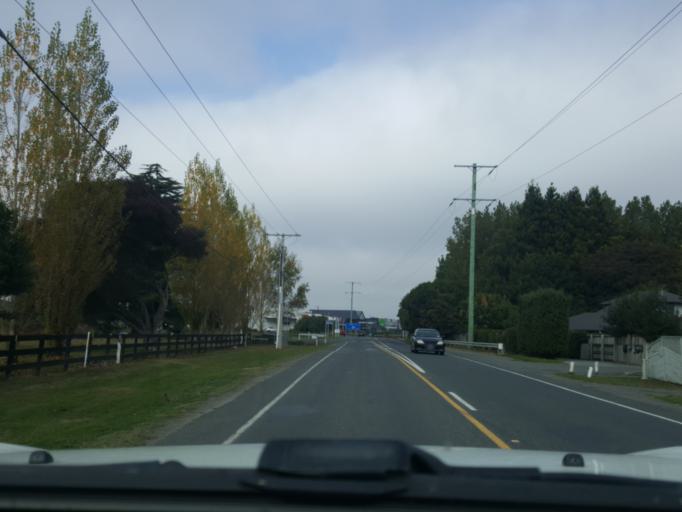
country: NZ
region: Waikato
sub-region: Hamilton City
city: Hamilton
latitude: -37.7476
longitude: 175.2929
